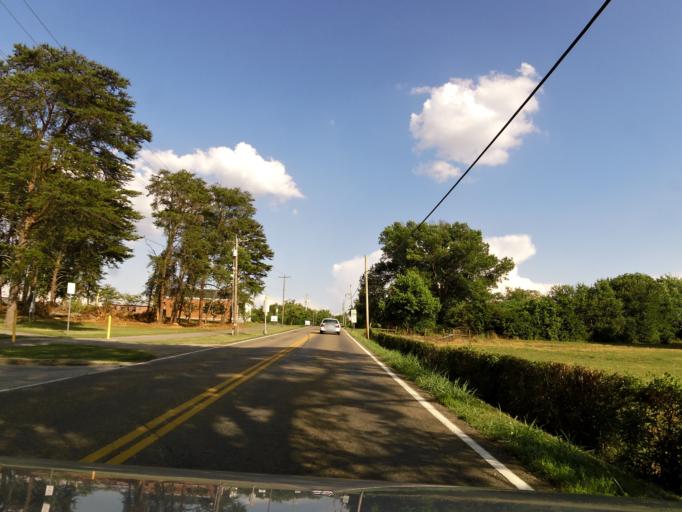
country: US
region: Tennessee
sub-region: Blount County
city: Alcoa
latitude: 35.7889
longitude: -83.9732
